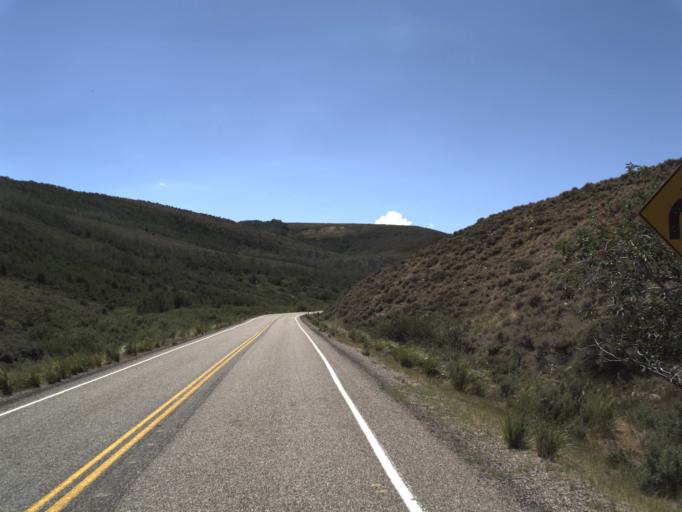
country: US
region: Utah
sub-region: Rich County
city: Randolph
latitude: 41.4790
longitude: -111.3540
